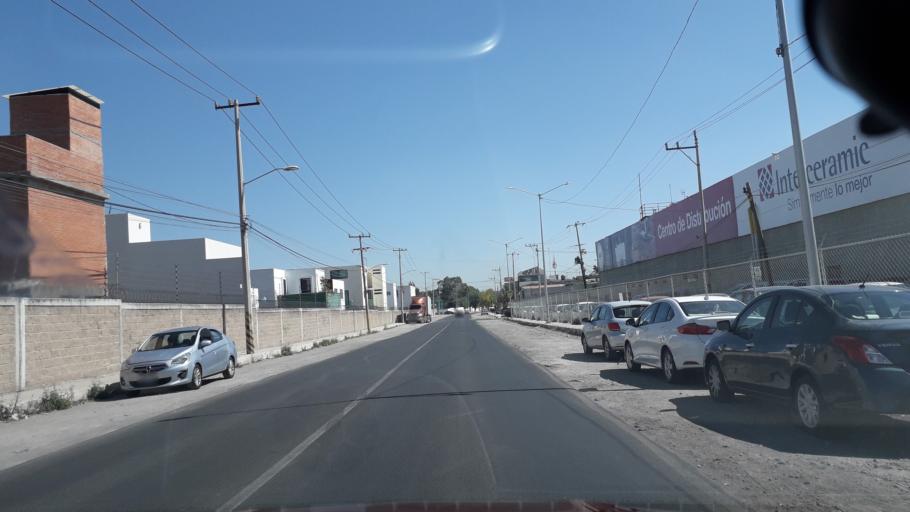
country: MX
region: Puebla
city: Puebla
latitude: 19.0820
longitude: -98.2158
